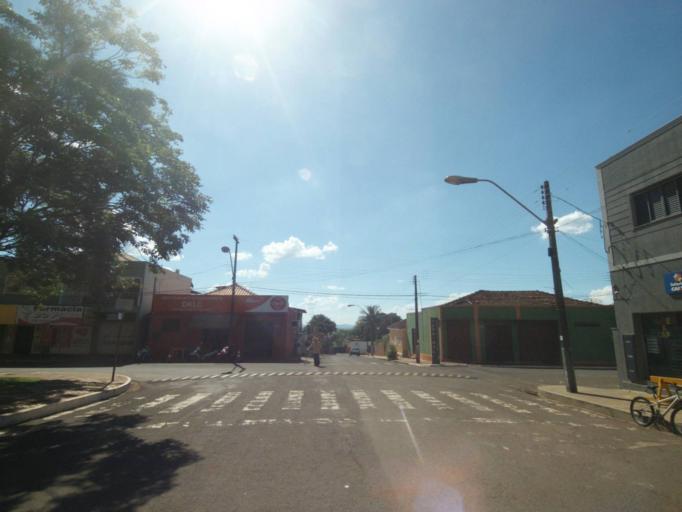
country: BR
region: Parana
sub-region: Sertanopolis
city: Sertanopolis
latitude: -23.0373
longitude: -50.8182
